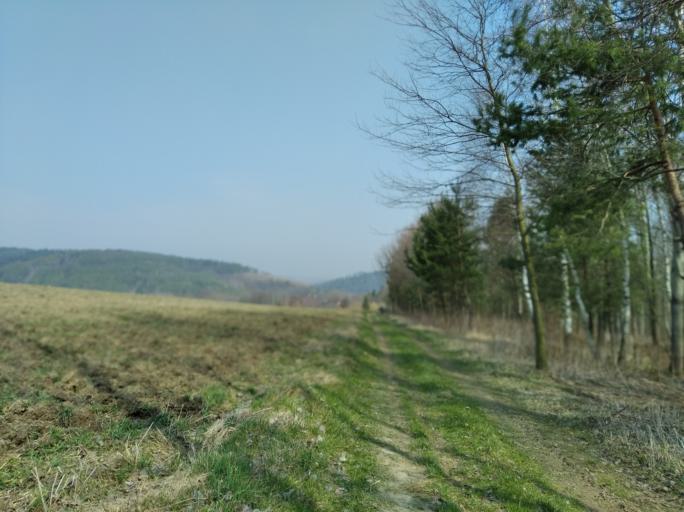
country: PL
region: Subcarpathian Voivodeship
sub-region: Powiat krosnienski
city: Korczyna
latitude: 49.7926
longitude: 21.8178
